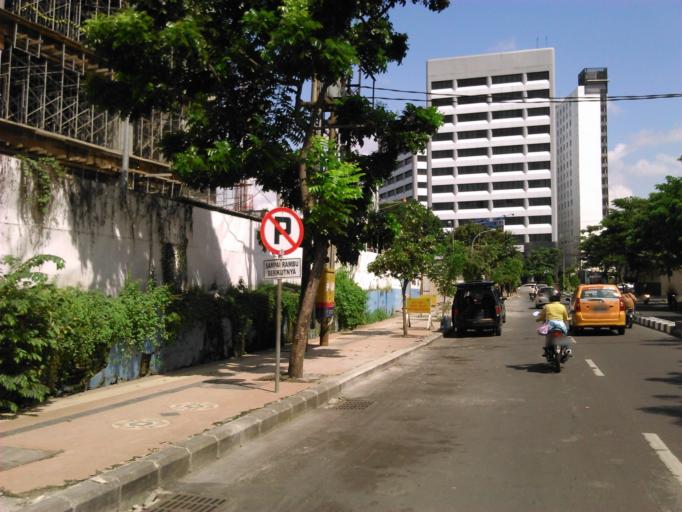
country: ID
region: East Java
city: Gubengairlangga
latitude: -7.2724
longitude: 112.7441
